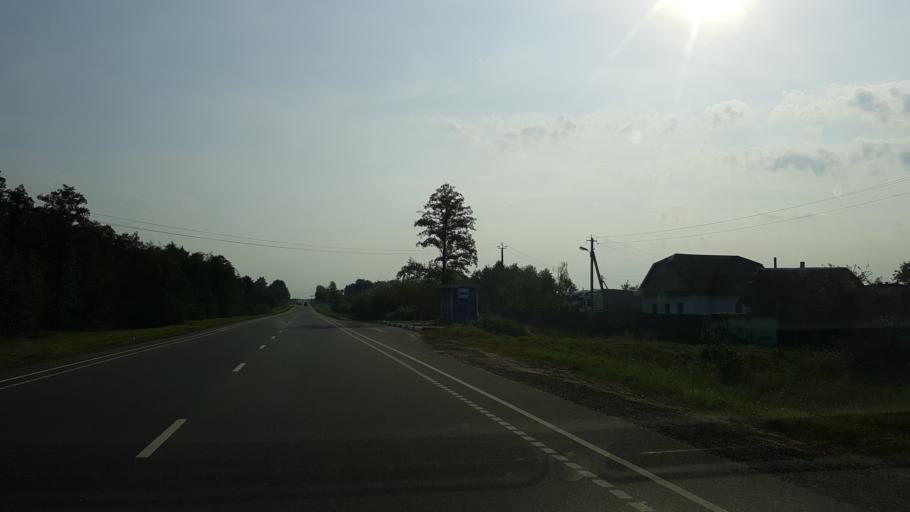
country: BY
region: Mogilev
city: Babruysk
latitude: 53.1414
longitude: 29.3449
